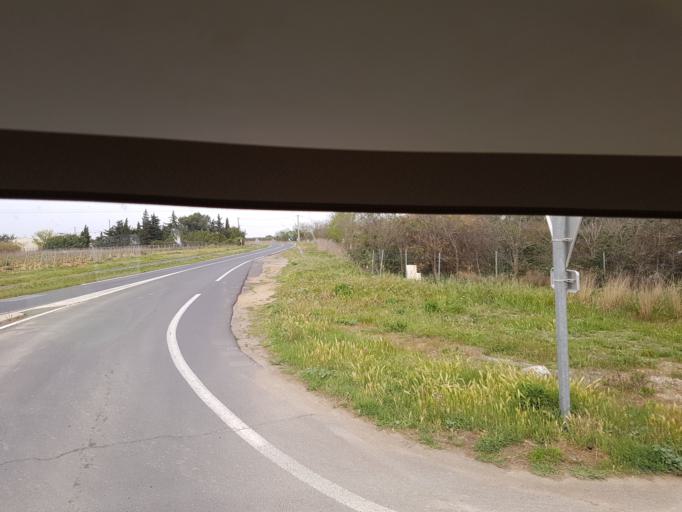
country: FR
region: Languedoc-Roussillon
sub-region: Departement de l'Herault
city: Serignan
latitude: 43.2718
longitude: 3.2606
